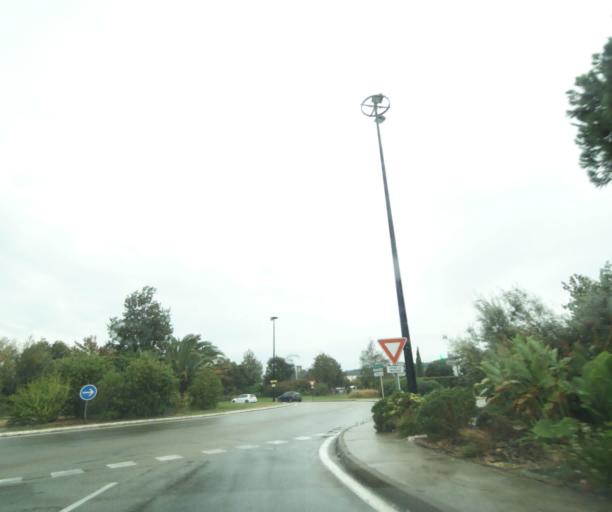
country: FR
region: Languedoc-Roussillon
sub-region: Departement du Gard
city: Rodilhan
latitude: 43.8575
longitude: 4.4051
